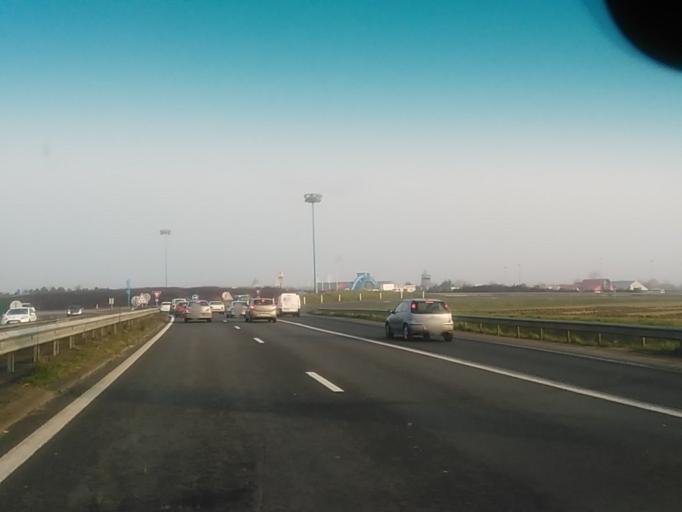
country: FR
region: Lower Normandy
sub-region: Departement du Calvados
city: Ifs
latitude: 49.1440
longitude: -0.3379
